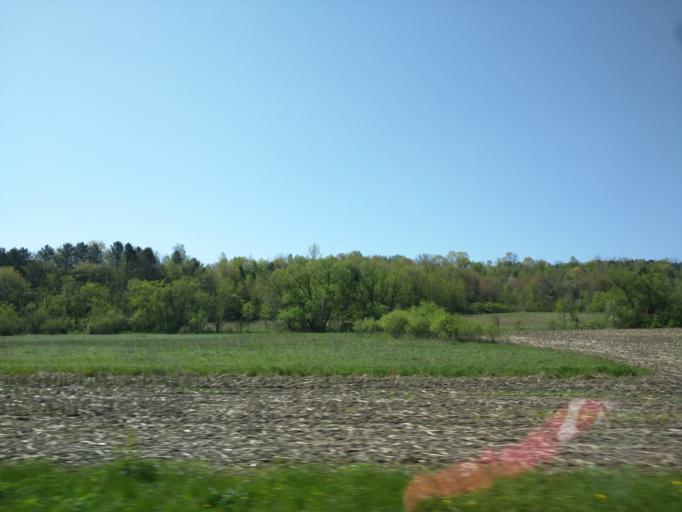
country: US
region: Wisconsin
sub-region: Monroe County
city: Cashton
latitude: 43.6319
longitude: -90.6531
